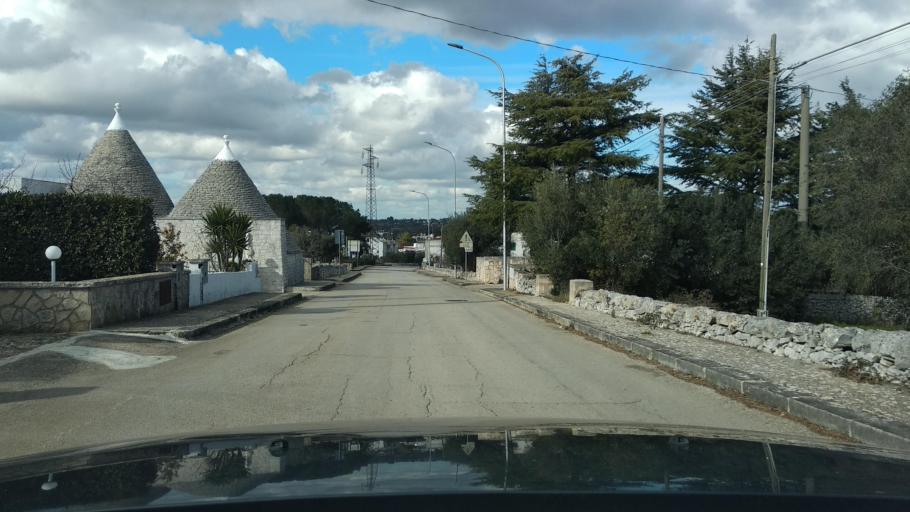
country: IT
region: Apulia
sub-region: Provincia di Brindisi
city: Cisternino
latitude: 40.7473
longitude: 17.4149
